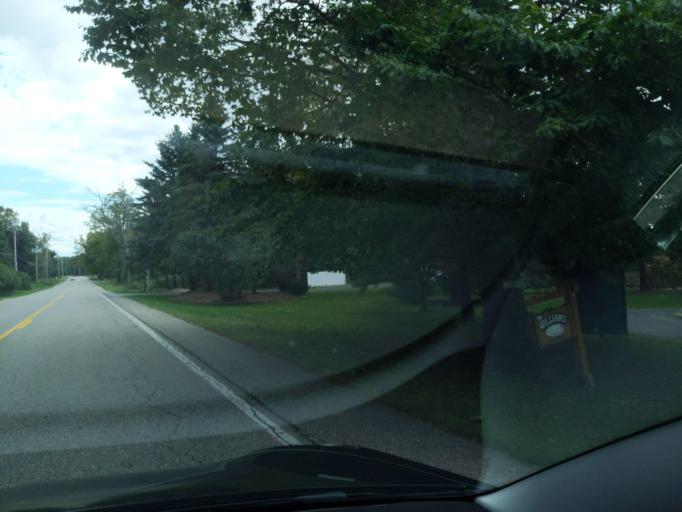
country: US
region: Michigan
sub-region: Kalkaska County
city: Rapid City
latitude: 44.9121
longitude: -85.2836
